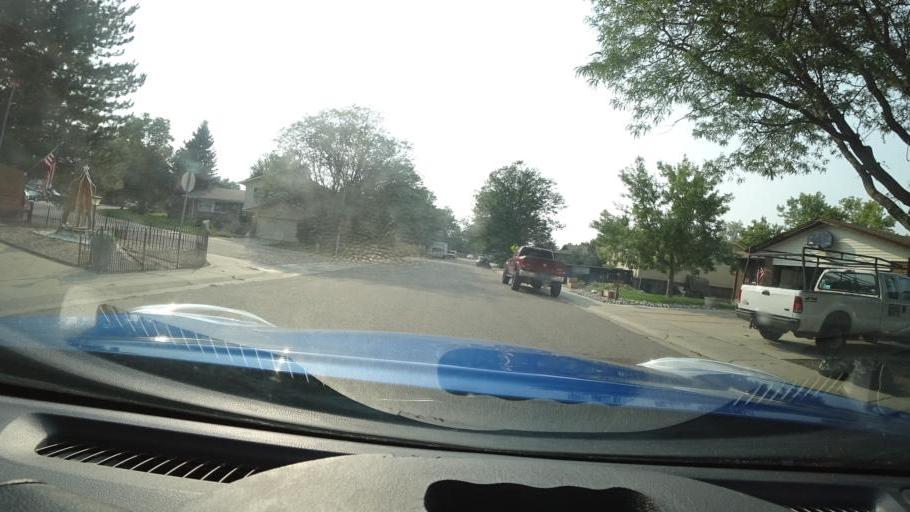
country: US
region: Colorado
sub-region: Adams County
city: Aurora
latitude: 39.6683
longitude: -104.7817
